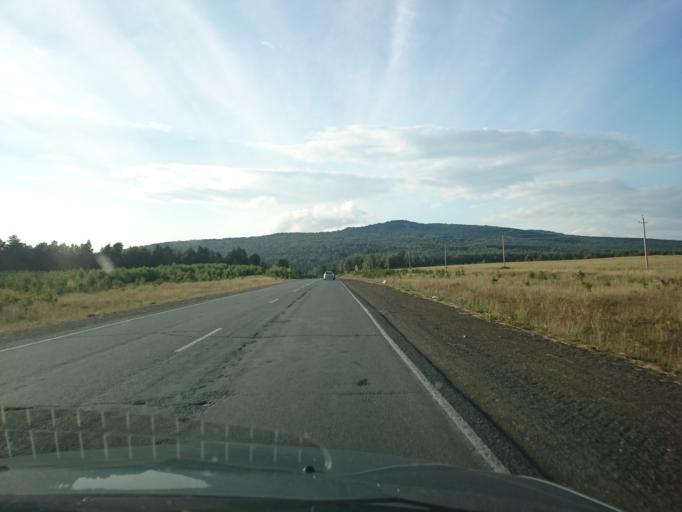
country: RU
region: Bashkortostan
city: Lomovka
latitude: 53.8914
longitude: 58.0948
